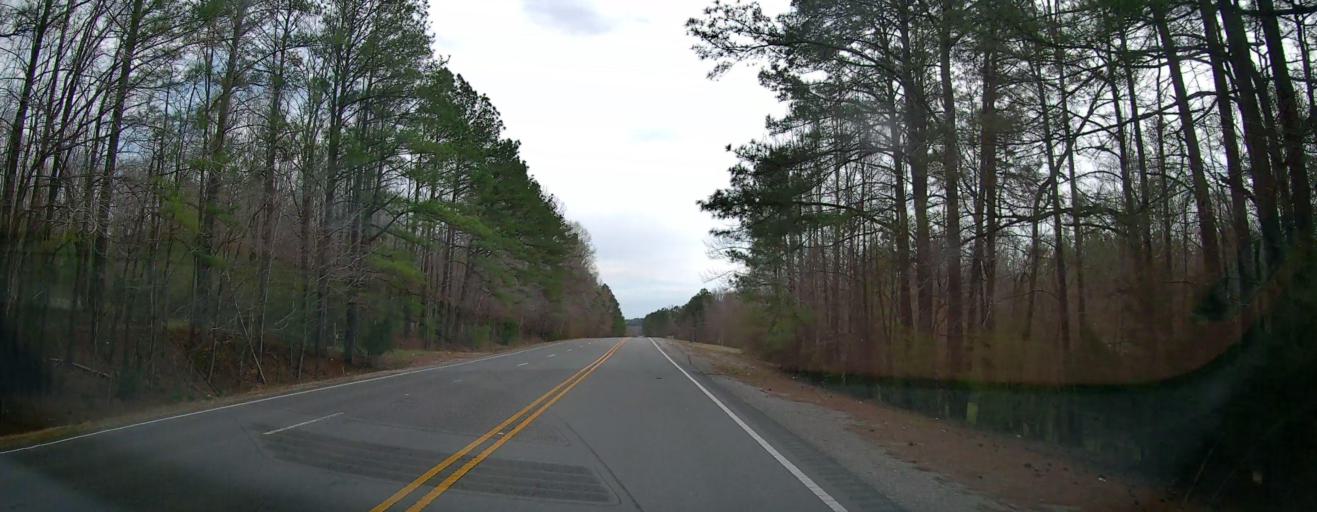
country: US
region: Alabama
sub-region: Marion County
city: Guin
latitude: 34.0176
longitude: -87.9376
